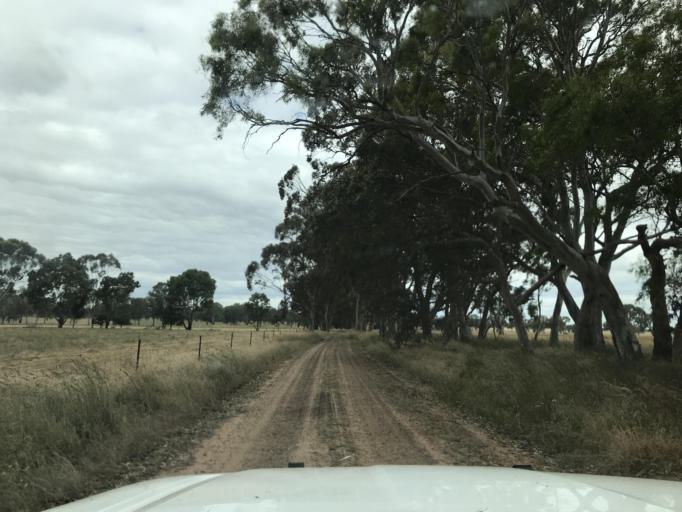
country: AU
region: South Australia
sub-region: Naracoorte and Lucindale
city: Naracoorte
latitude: -36.9244
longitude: 141.3031
